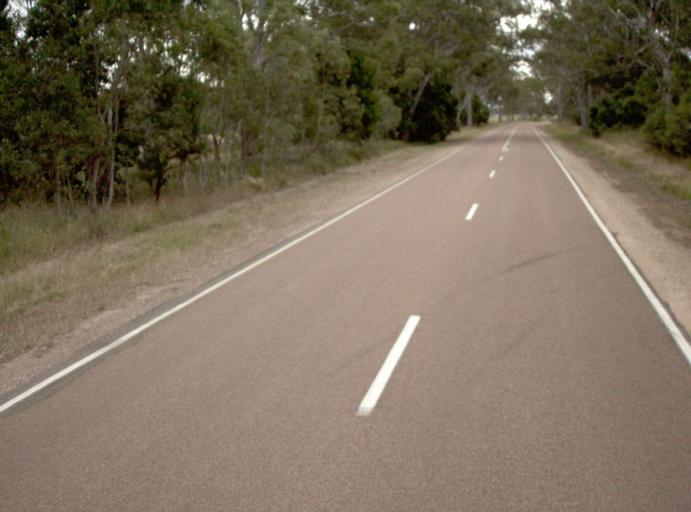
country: AU
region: Victoria
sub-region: Wellington
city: Sale
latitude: -38.0017
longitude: 147.3160
